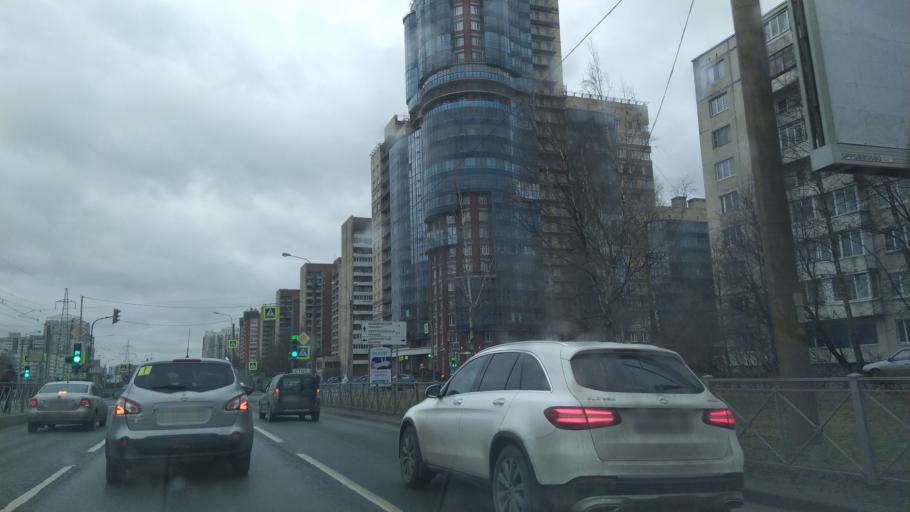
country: RU
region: St.-Petersburg
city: Komendantsky aerodrom
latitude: 60.0053
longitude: 30.2813
